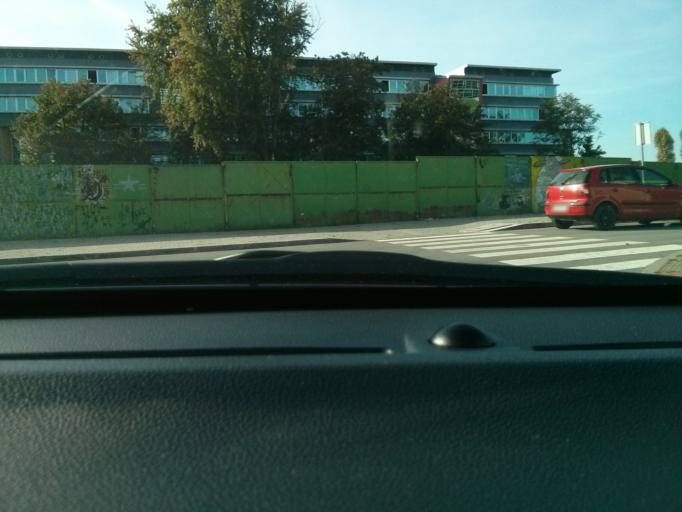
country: HR
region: Osjecko-Baranjska
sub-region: Grad Osijek
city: Osijek
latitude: 45.5558
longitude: 18.7064
